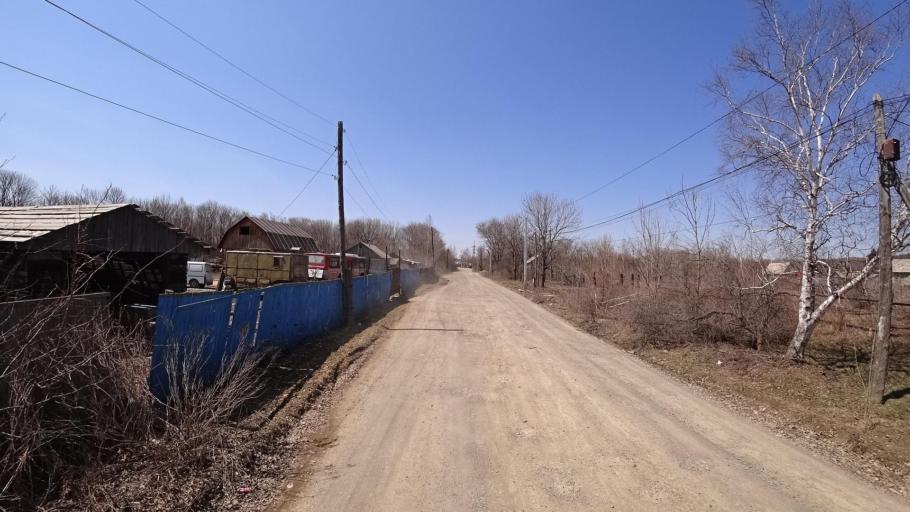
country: RU
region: Khabarovsk Krai
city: Khurba
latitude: 50.4095
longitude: 136.8630
